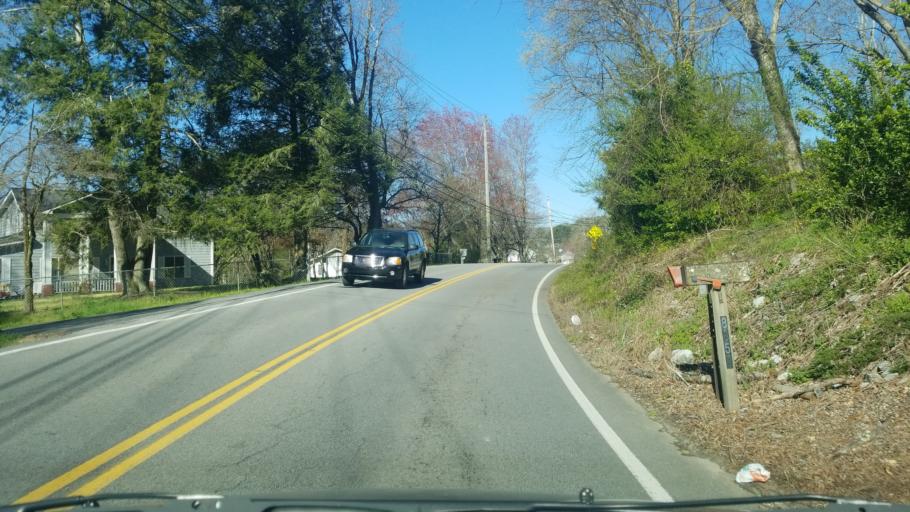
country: US
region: Tennessee
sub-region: Hamilton County
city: Middle Valley
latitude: 35.2151
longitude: -85.1849
